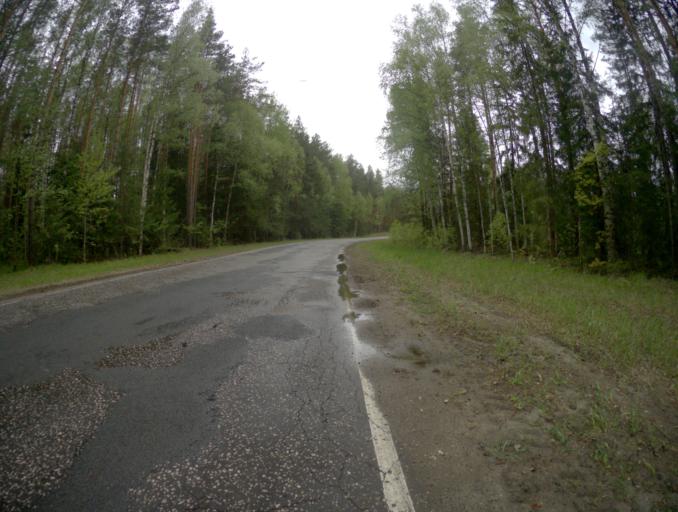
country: RU
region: Vladimir
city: Velikodvorskiy
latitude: 55.3945
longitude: 40.7093
